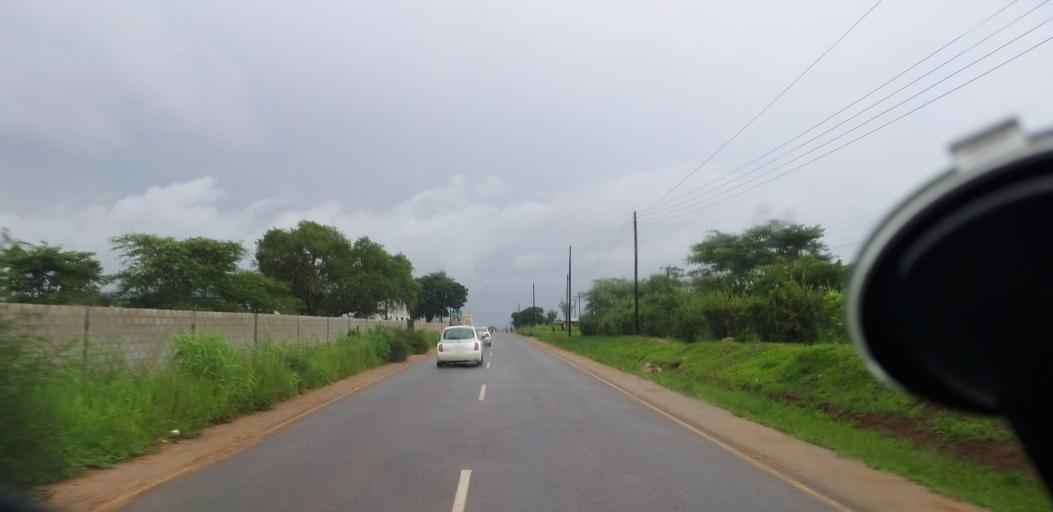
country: ZM
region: Lusaka
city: Lusaka
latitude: -15.5112
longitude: 28.3115
